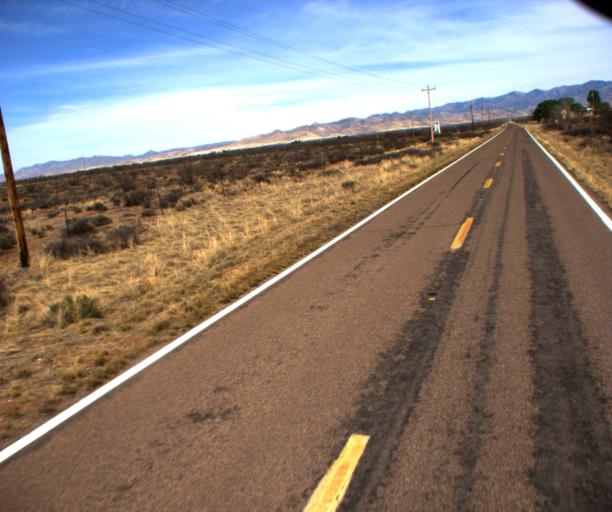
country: US
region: Arizona
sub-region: Cochise County
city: Willcox
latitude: 31.8760
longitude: -109.5787
